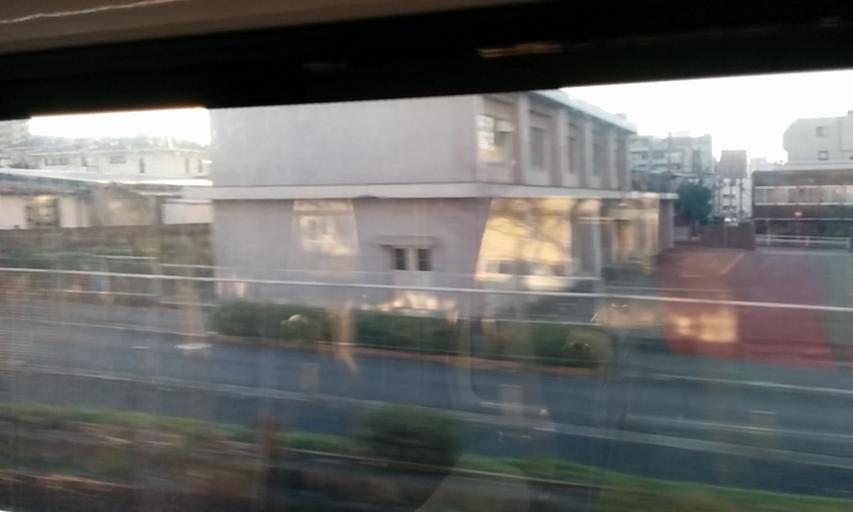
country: JP
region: Aichi
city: Nagoya-shi
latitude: 35.1852
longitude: 136.9371
